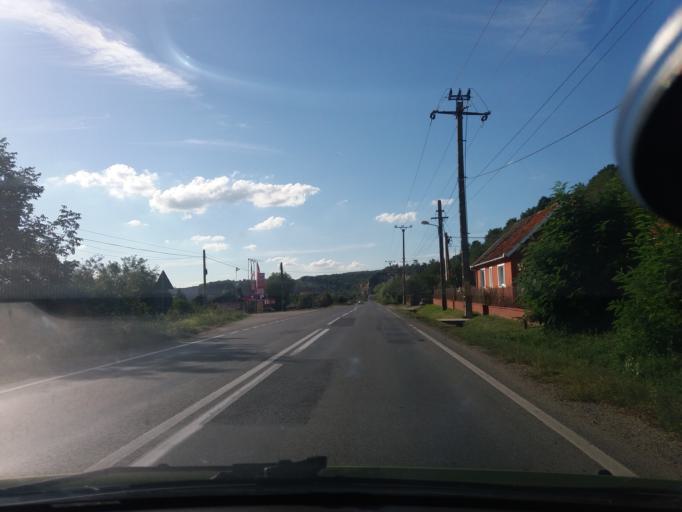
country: RO
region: Arad
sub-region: Oras Lipova
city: Radna
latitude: 46.1020
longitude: 21.6628
